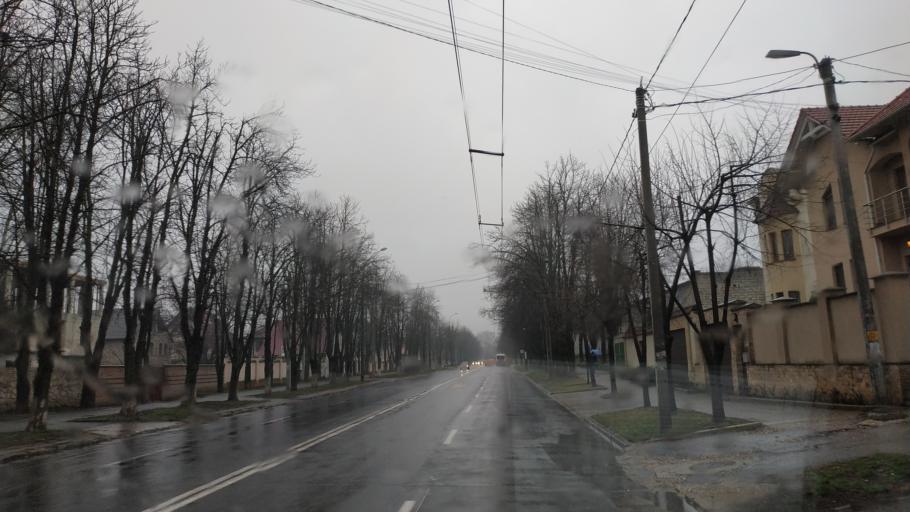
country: MD
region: Chisinau
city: Chisinau
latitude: 47.0258
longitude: 28.8028
